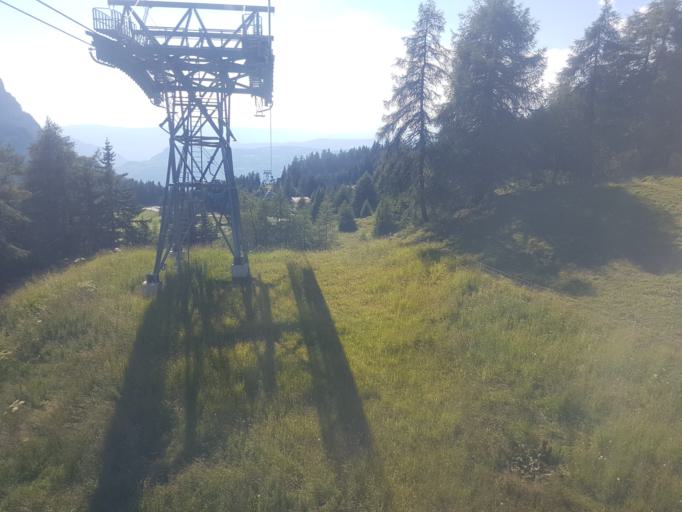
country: IT
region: Trentino-Alto Adige
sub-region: Bolzano
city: Siusi
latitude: 46.5423
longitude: 11.6132
